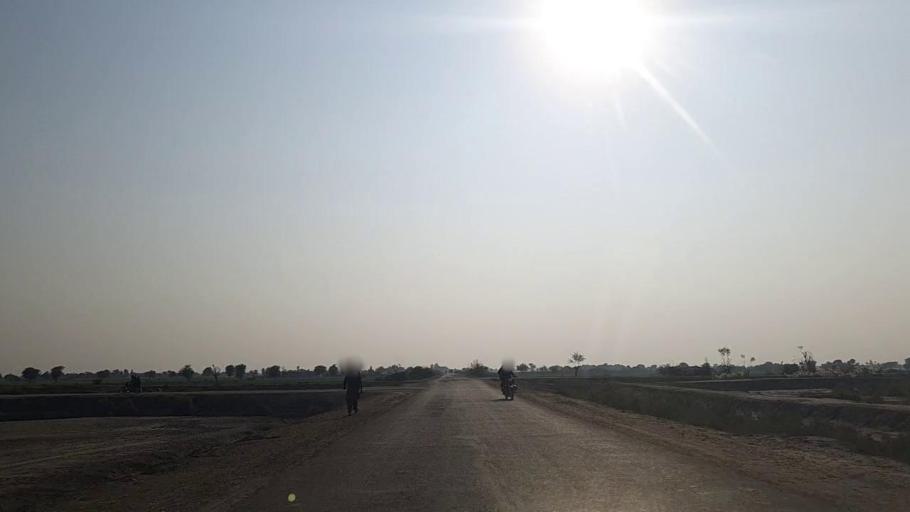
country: PK
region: Sindh
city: Jam Sahib
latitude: 26.2862
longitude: 68.6234
